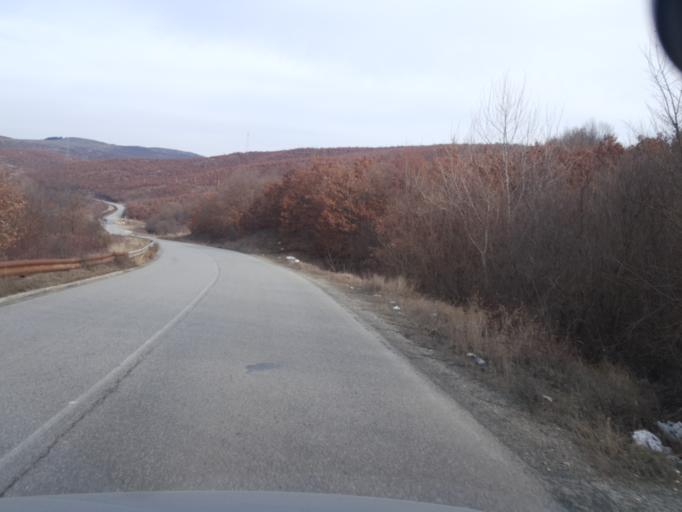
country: XK
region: Pec
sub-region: Komuna e Pejes
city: Kosuriq
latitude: 42.5145
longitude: 20.5514
